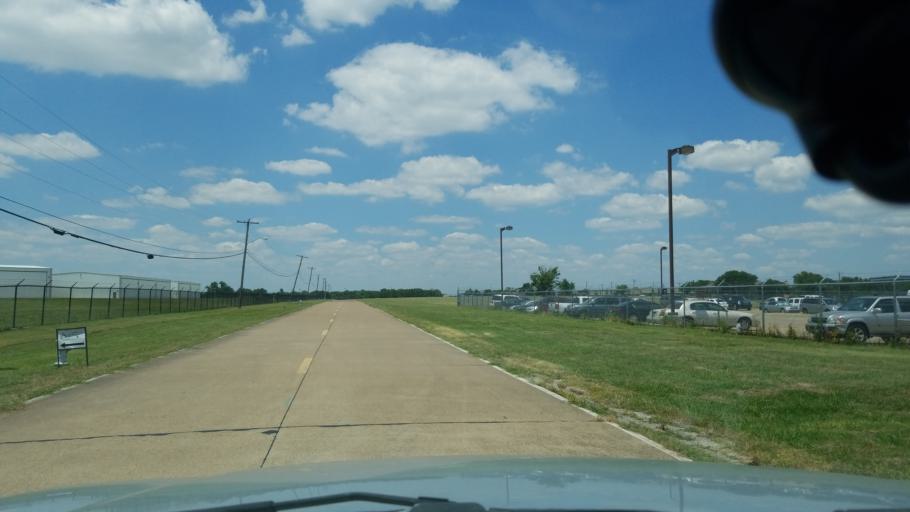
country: US
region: Texas
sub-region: Dallas County
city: Duncanville
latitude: 32.6791
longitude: -96.8590
